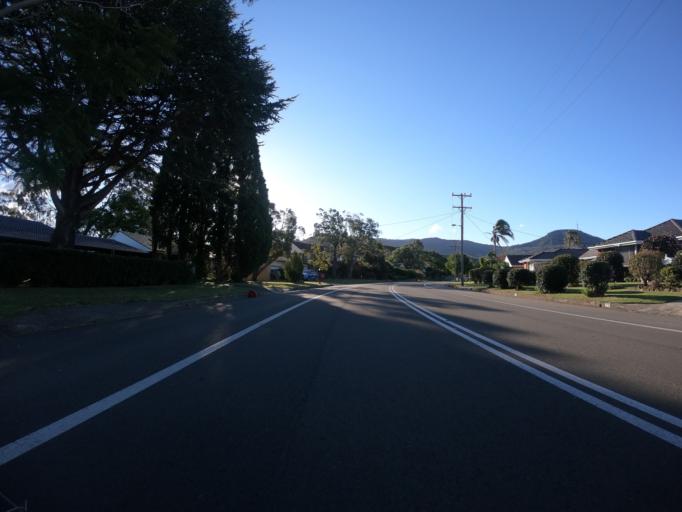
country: AU
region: New South Wales
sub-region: Wollongong
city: Mount Keira
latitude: -34.4305
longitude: 150.8478
